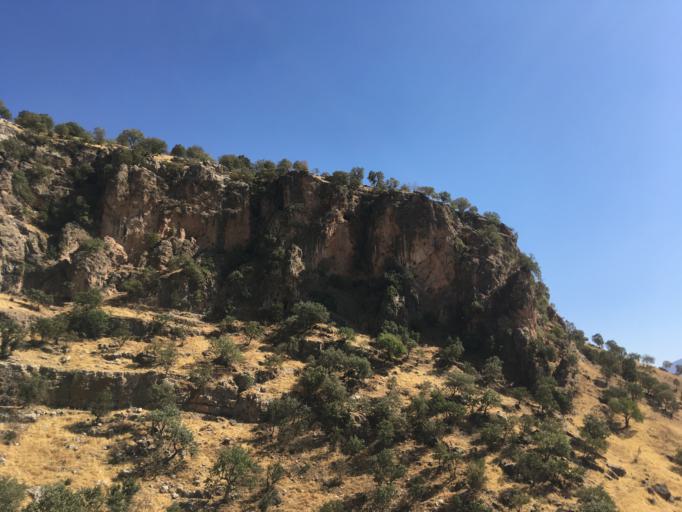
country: IQ
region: Arbil
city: Mergasur
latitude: 36.8346
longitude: 44.2191
